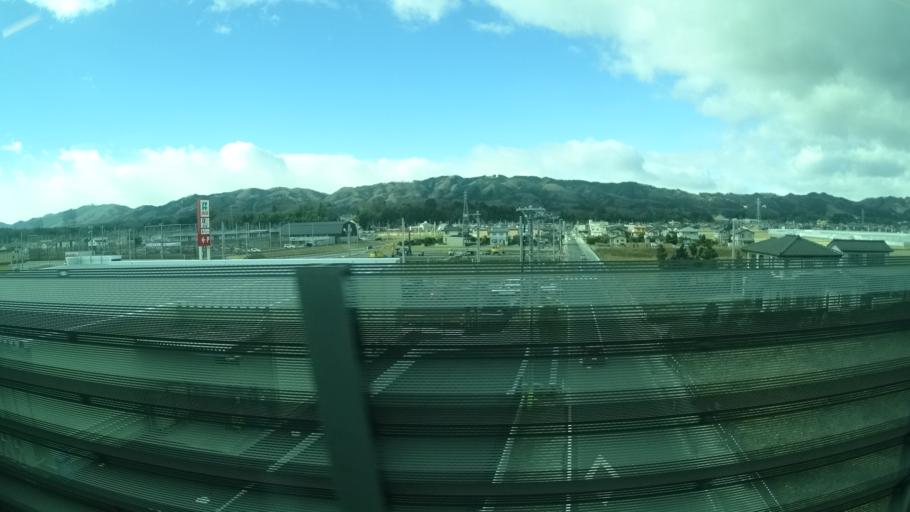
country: JP
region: Miyagi
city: Watari
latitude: 37.9672
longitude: 140.8887
